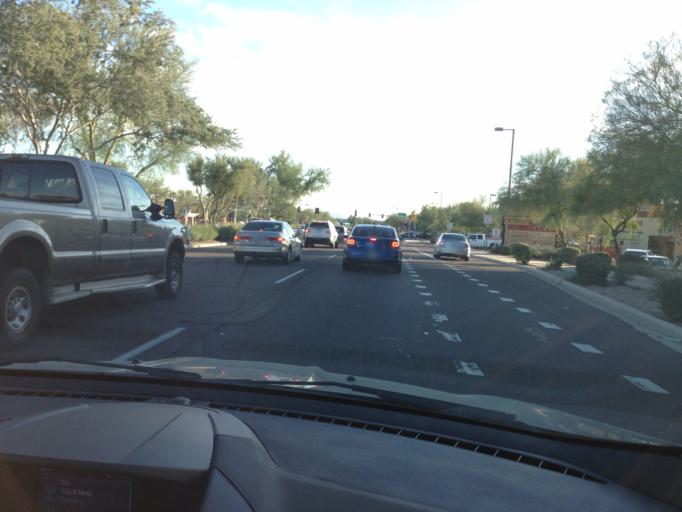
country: US
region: Arizona
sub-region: Maricopa County
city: Paradise Valley
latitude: 33.6785
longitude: -111.9776
